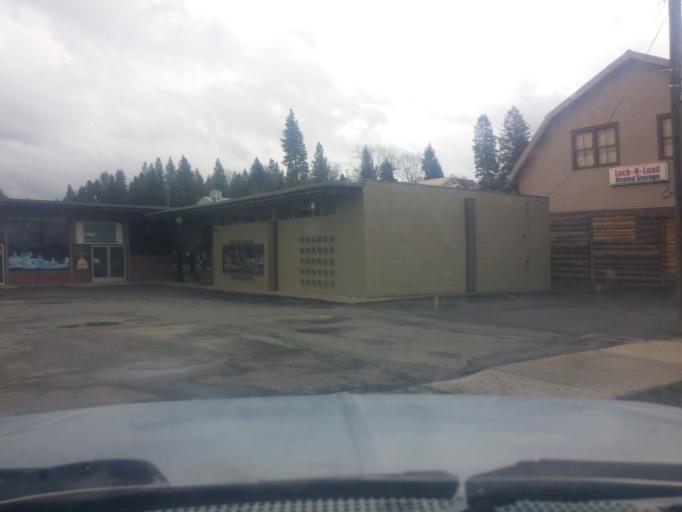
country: US
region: Idaho
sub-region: Latah County
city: Moscow
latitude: 46.9213
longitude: -116.9005
